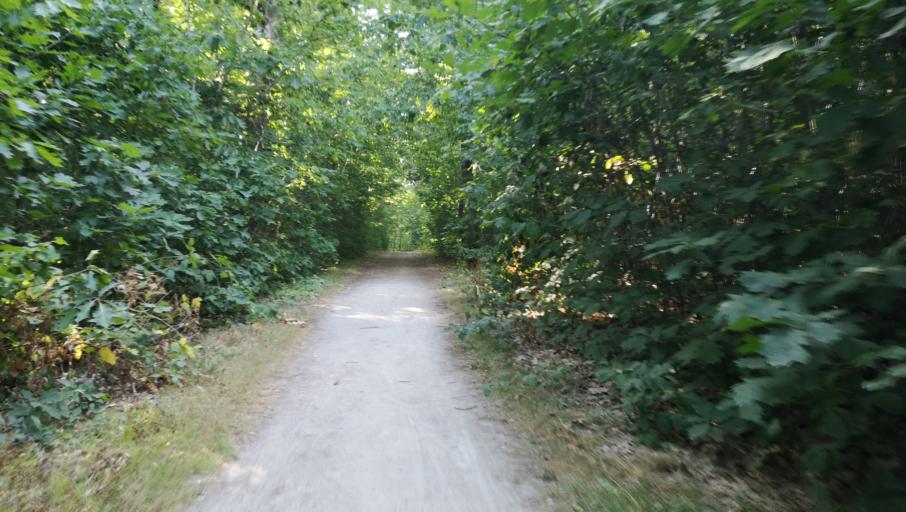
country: FR
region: Centre
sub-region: Departement du Loiret
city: Saint-Jean-de-Braye
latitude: 47.9368
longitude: 1.9831
